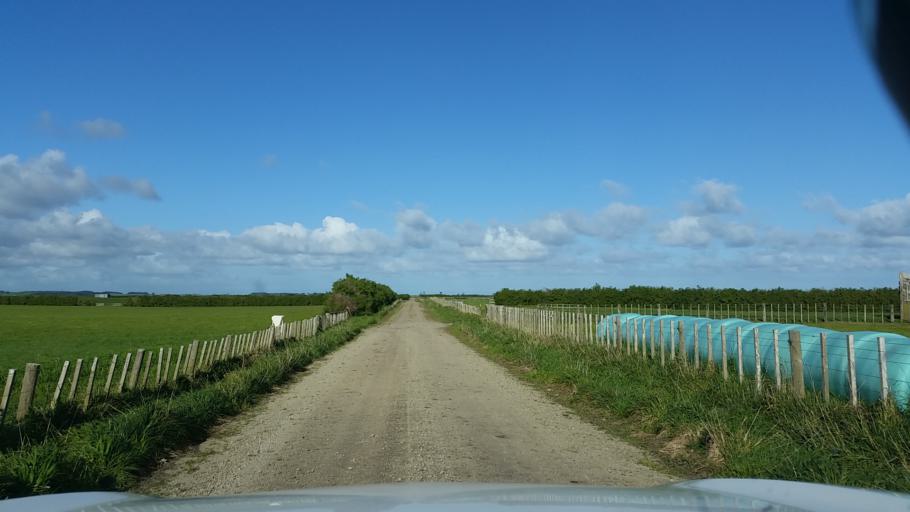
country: NZ
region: Taranaki
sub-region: South Taranaki District
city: Patea
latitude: -39.7483
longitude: 174.5174
